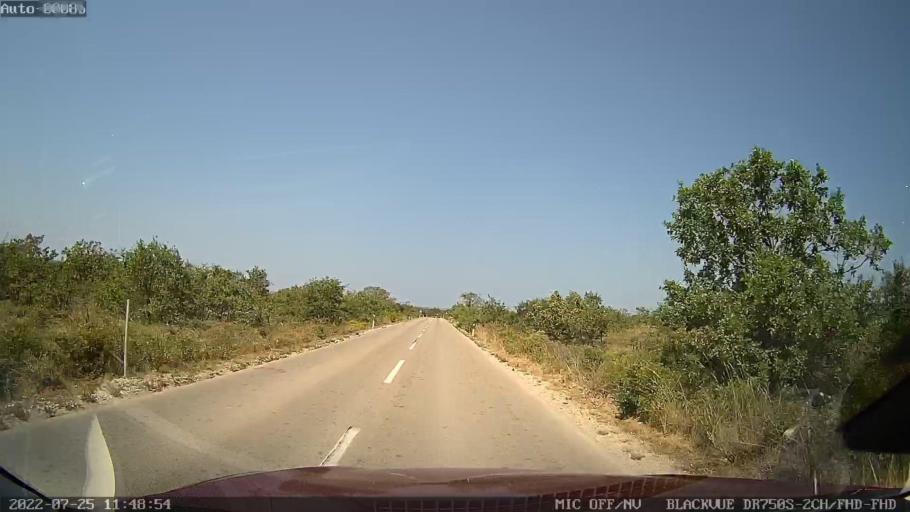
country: HR
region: Zadarska
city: Vrsi
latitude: 44.2348
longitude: 15.2912
